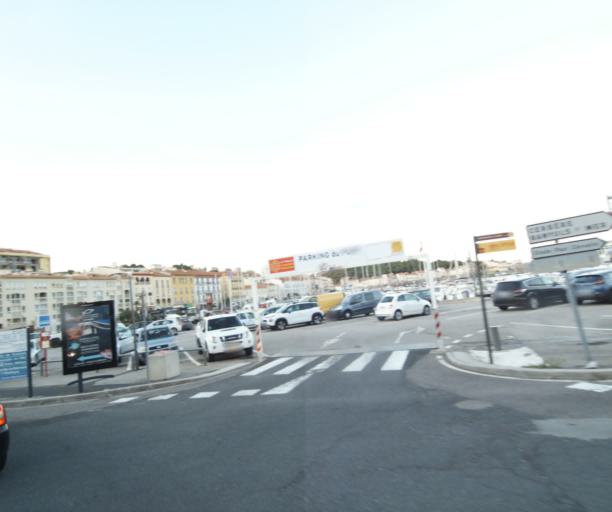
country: FR
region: Languedoc-Roussillon
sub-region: Departement des Pyrenees-Orientales
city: Portvendres
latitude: 42.5160
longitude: 3.1061
